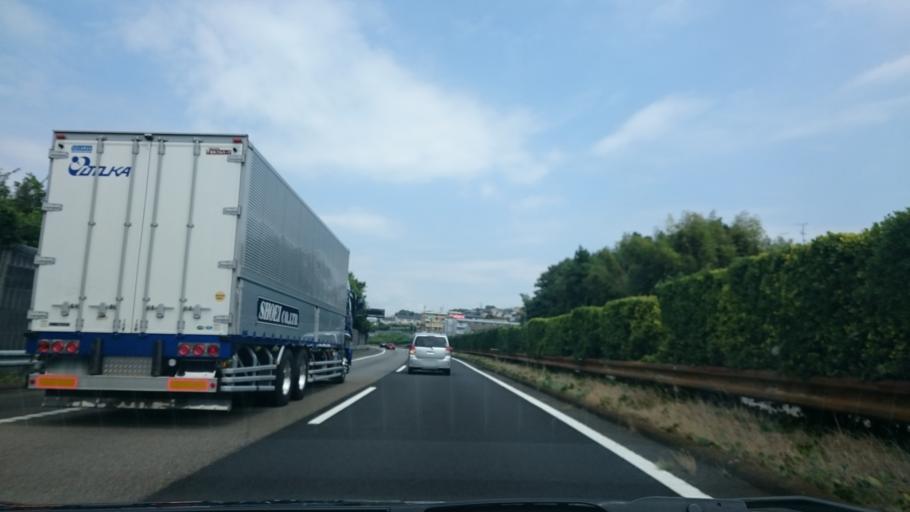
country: JP
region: Shizuoka
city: Shizuoka-shi
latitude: 34.9669
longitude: 138.4285
